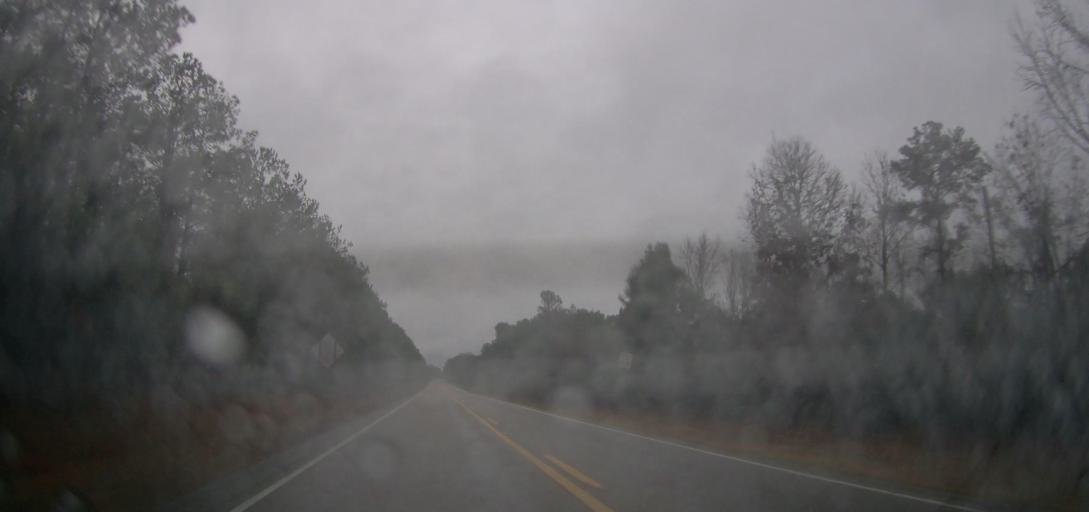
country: US
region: Alabama
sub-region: Autauga County
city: Pine Level
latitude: 32.5513
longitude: -86.6539
